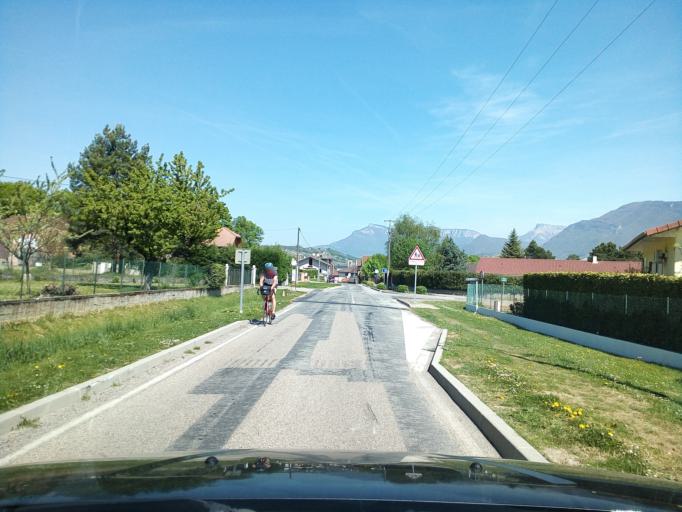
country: FR
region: Rhone-Alpes
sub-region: Departement de l'Isere
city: Chapareillan
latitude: 45.4591
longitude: 5.9908
